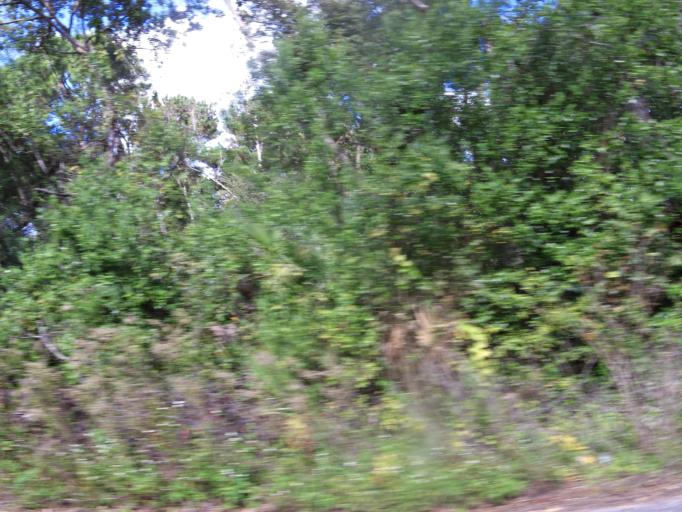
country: US
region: Florida
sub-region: Duval County
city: Jacksonville
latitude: 30.4101
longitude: -81.6413
